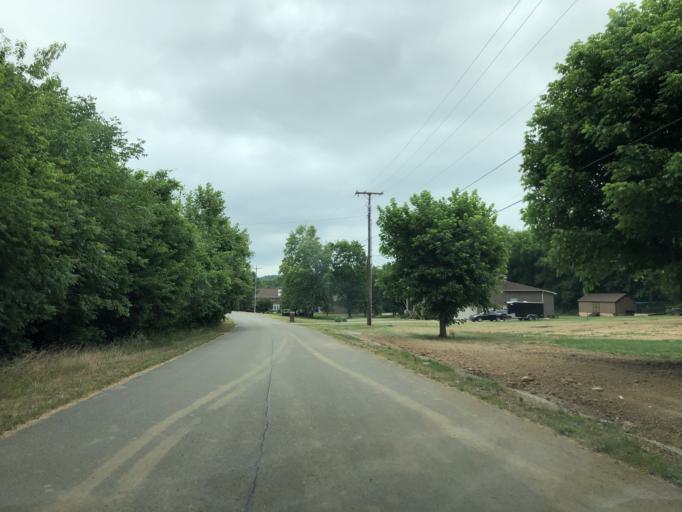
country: US
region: Tennessee
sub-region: Davidson County
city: Goodlettsville
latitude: 36.2744
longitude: -86.7828
